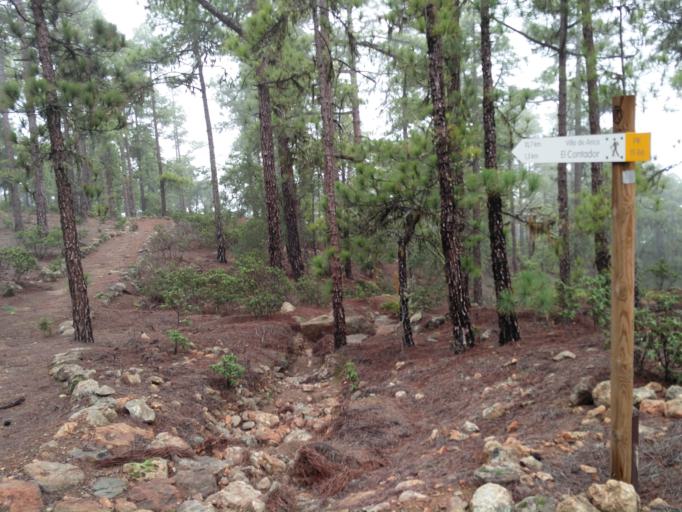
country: ES
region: Canary Islands
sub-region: Provincia de Santa Cruz de Tenerife
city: Lomo de Arico
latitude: 28.2056
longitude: -16.5472
